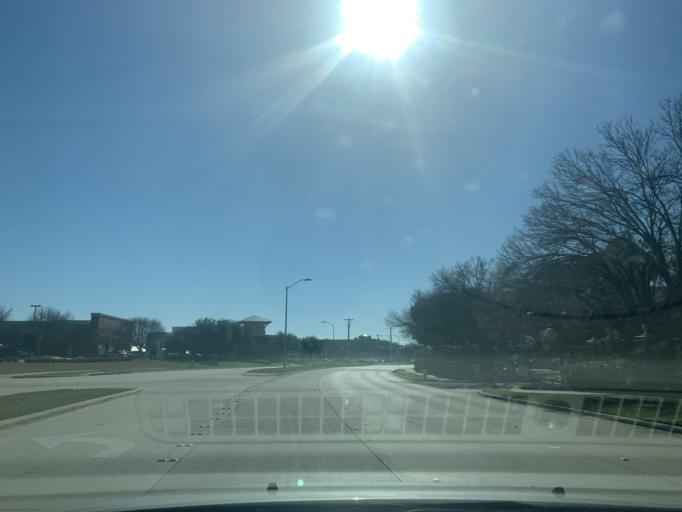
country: US
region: Texas
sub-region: Denton County
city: The Colony
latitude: 33.0575
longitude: -96.8330
